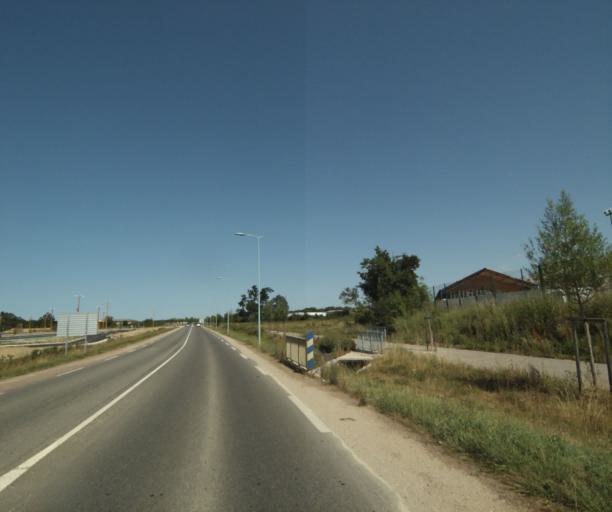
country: FR
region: Midi-Pyrenees
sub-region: Departement du Tarn-et-Garonne
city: Montauban
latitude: 44.0438
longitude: 1.3826
